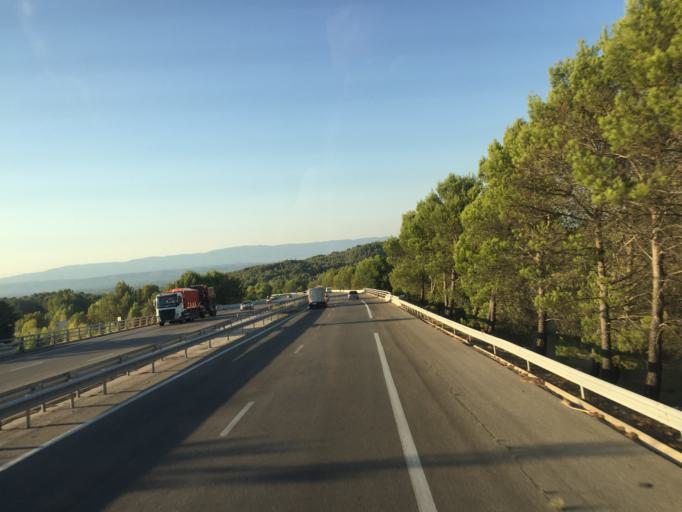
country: FR
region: Provence-Alpes-Cote d'Azur
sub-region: Departement des Bouches-du-Rhone
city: Venelles
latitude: 43.6089
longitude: 5.4975
